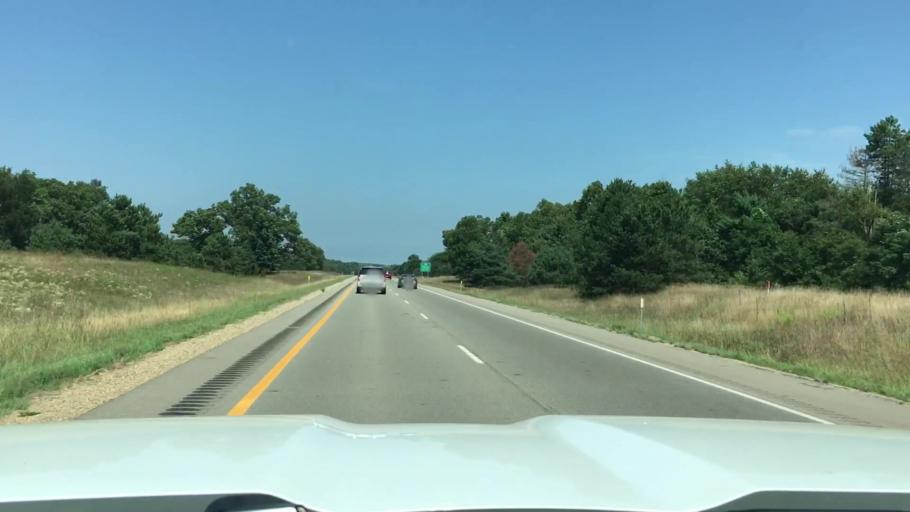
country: US
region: Michigan
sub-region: Kalamazoo County
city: Portage
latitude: 42.1844
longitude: -85.6457
